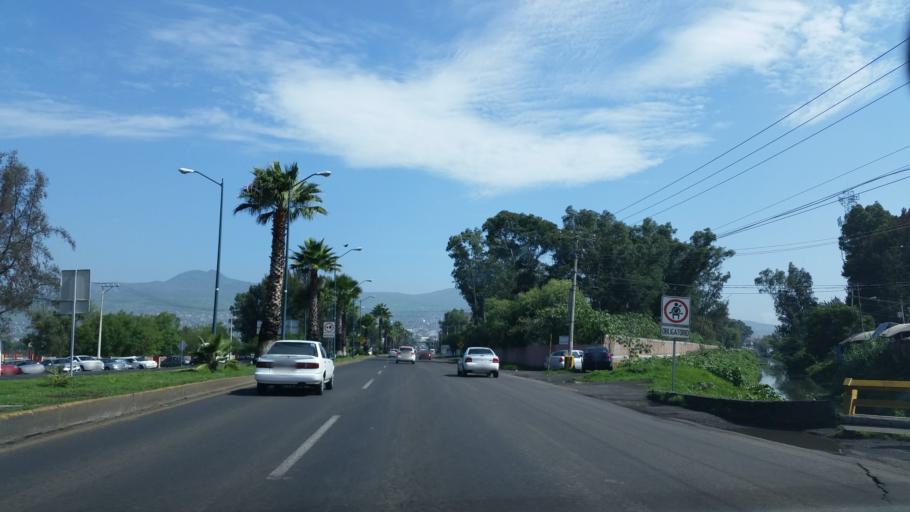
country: MX
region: Michoacan
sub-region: Morelia
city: Morelos
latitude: 19.6819
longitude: -101.2356
